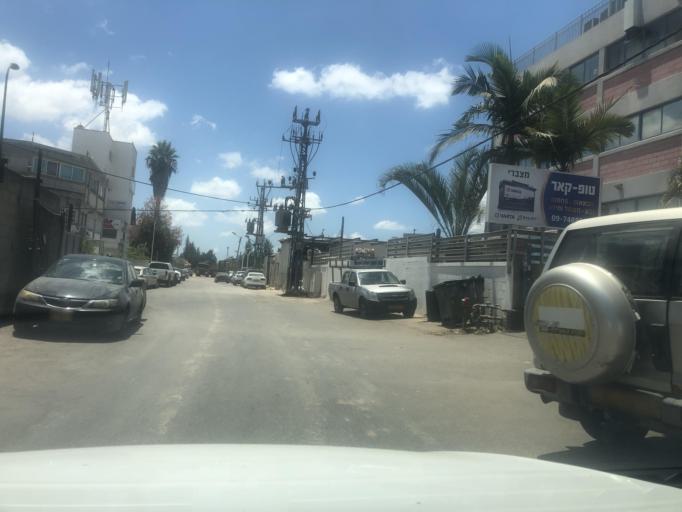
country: IL
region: Central District
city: Kfar Saba
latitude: 32.1556
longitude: 34.9207
